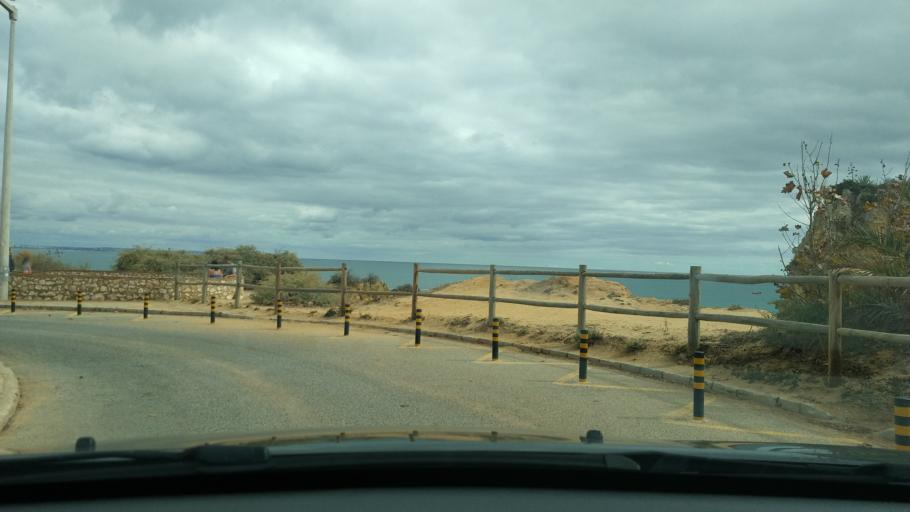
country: PT
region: Faro
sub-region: Lagos
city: Lagos
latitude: 37.0912
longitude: -8.6700
